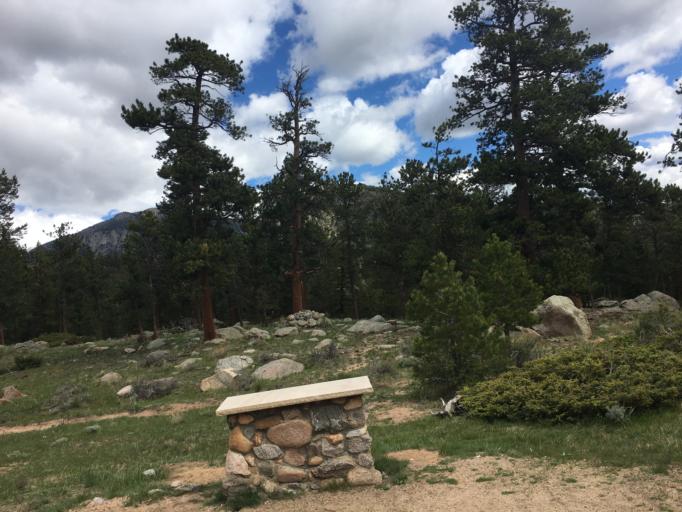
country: US
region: Colorado
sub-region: Larimer County
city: Estes Park
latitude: 40.3431
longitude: -105.5816
